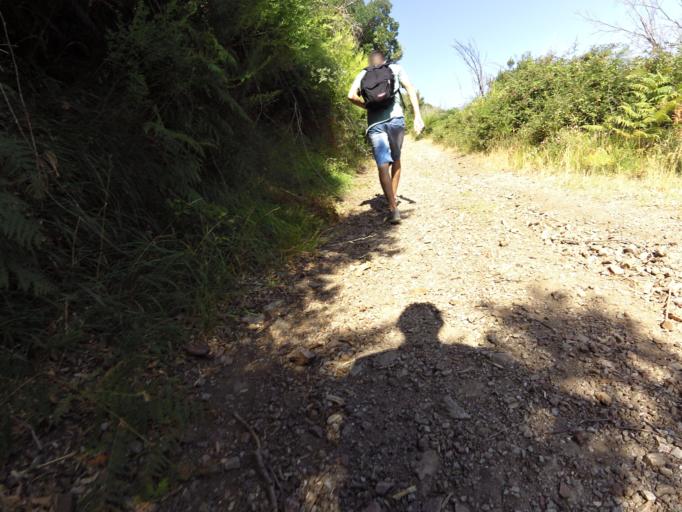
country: IT
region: Calabria
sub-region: Provincia di Reggio Calabria
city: Bivongi
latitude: 38.5010
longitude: 16.4492
